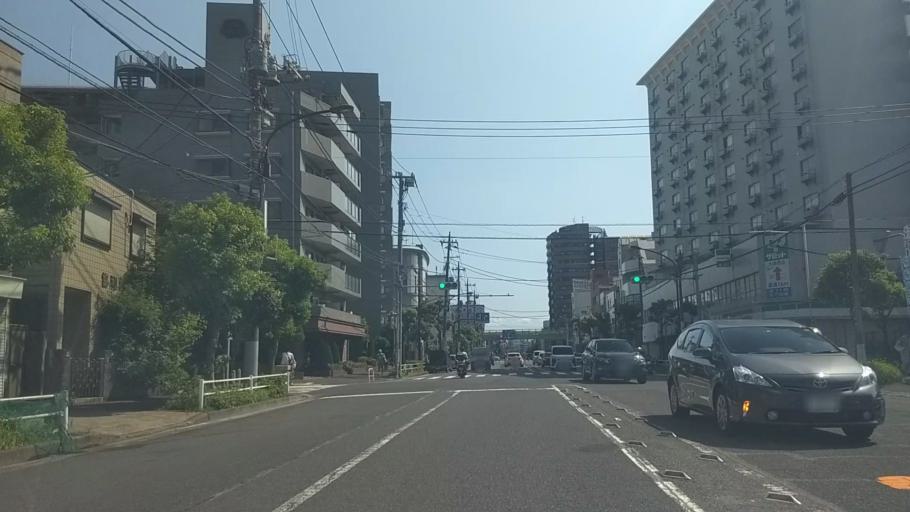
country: JP
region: Kanagawa
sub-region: Kawasaki-shi
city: Kawasaki
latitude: 35.5810
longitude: 139.7288
